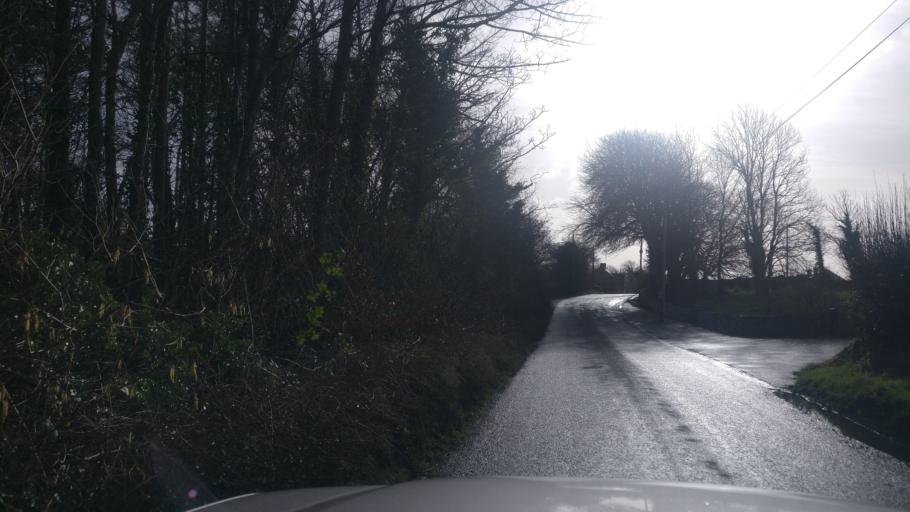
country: IE
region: Connaught
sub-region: County Galway
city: Loughrea
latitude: 53.2791
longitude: -8.5827
